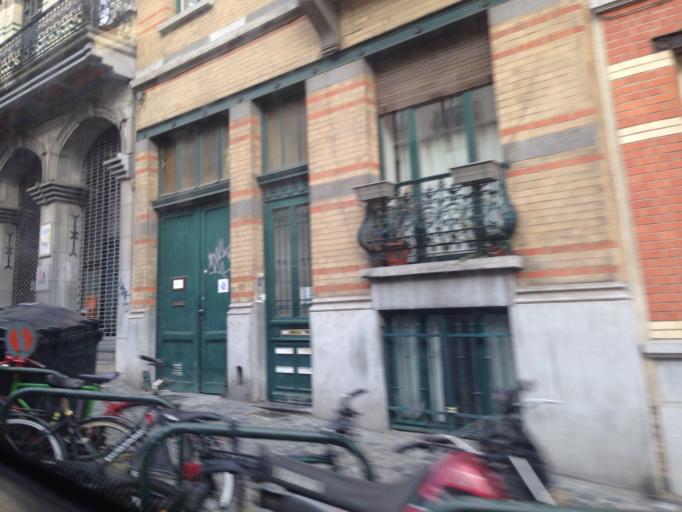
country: BE
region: Brussels Capital
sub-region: Bruxelles-Capitale
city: Brussels
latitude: 50.8347
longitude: 4.3794
